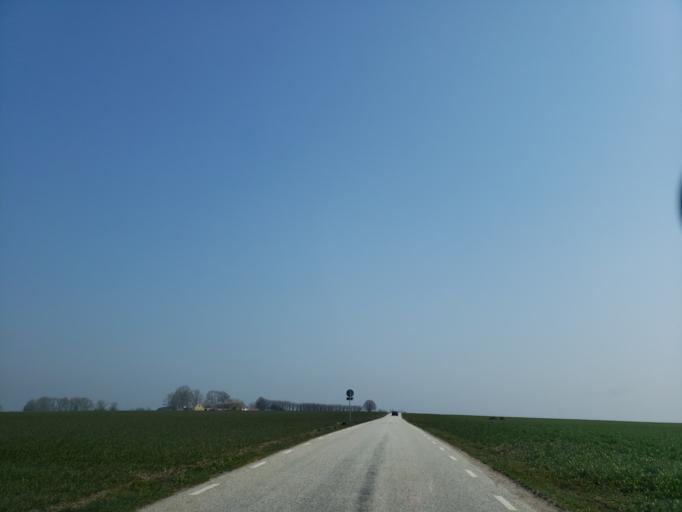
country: SE
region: Skane
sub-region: Simrishamns Kommun
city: Simrishamn
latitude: 55.5064
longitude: 14.3014
